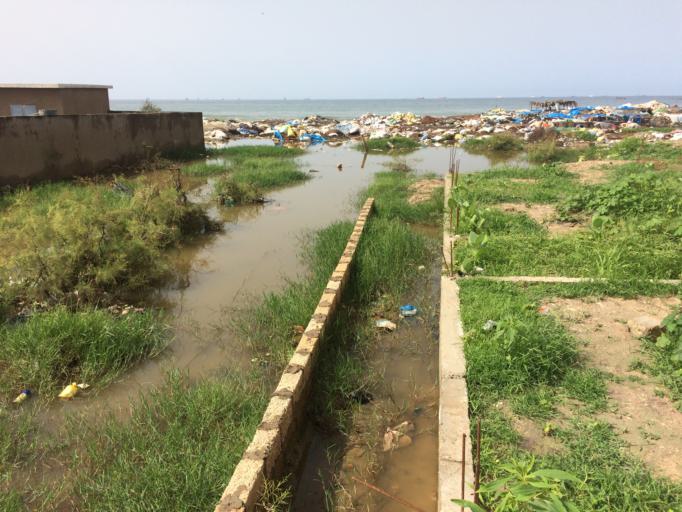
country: SN
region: Dakar
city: Pikine
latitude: 14.7269
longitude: -17.3181
